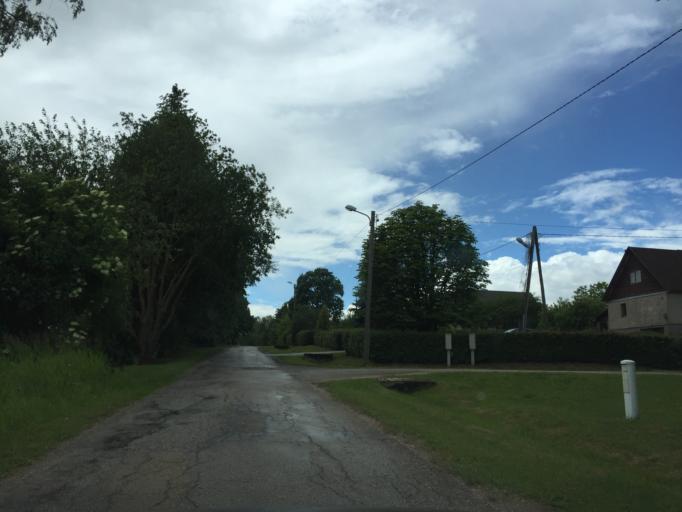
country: LV
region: Lecava
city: Iecava
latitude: 56.5613
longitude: 24.1625
